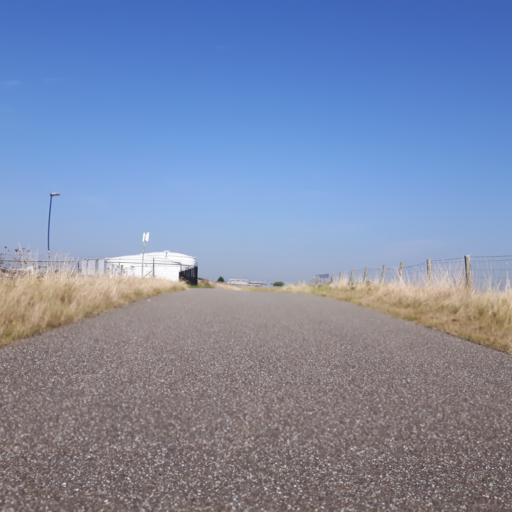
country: NL
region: Zeeland
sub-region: Gemeente Vlissingen
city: Vlissingen
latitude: 51.4450
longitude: 3.6034
